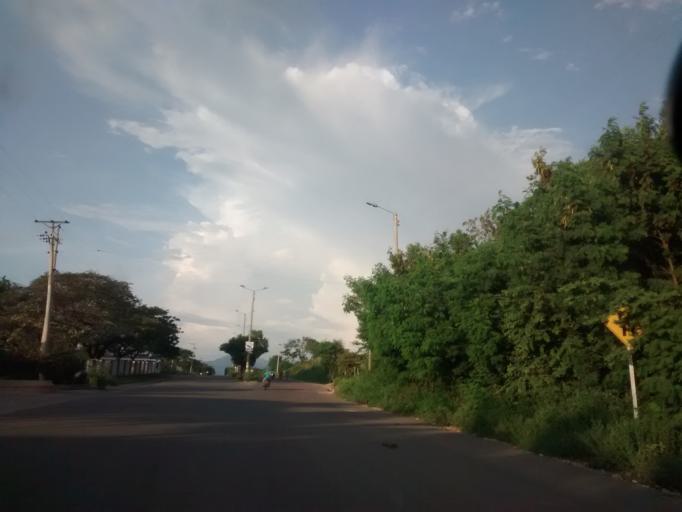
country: CO
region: Cundinamarca
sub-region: Girardot
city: Girardot City
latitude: 4.3137
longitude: -74.8088
